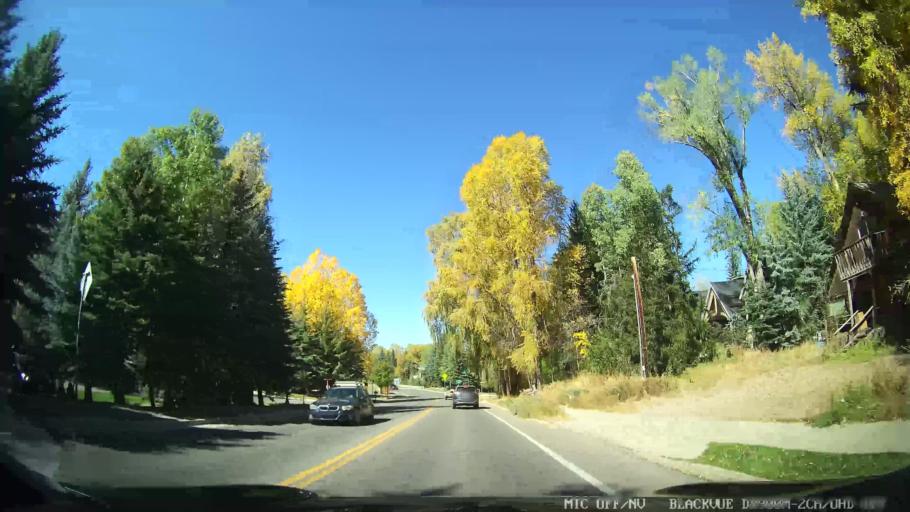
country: US
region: Colorado
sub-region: Pitkin County
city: Aspen
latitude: 39.1856
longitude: -106.8089
